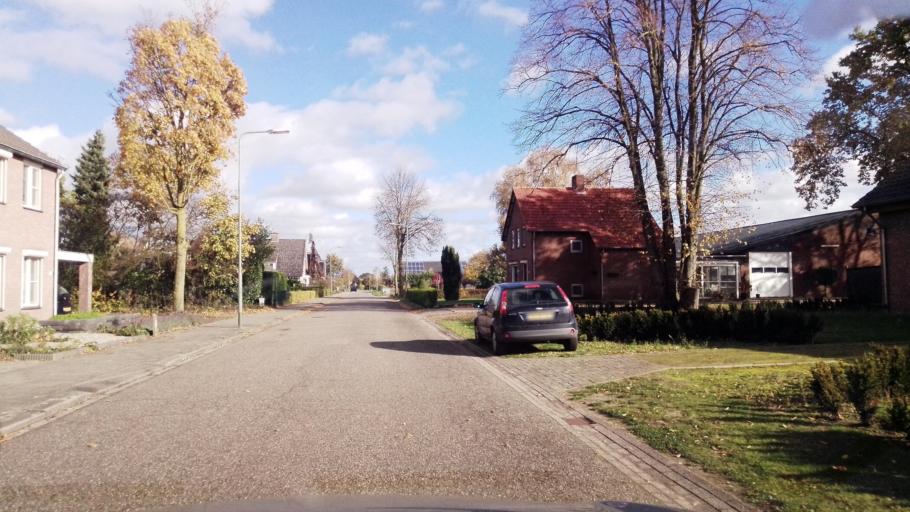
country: NL
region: Limburg
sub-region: Gemeente Bergen
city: Wellerlooi
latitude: 51.4591
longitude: 6.0873
